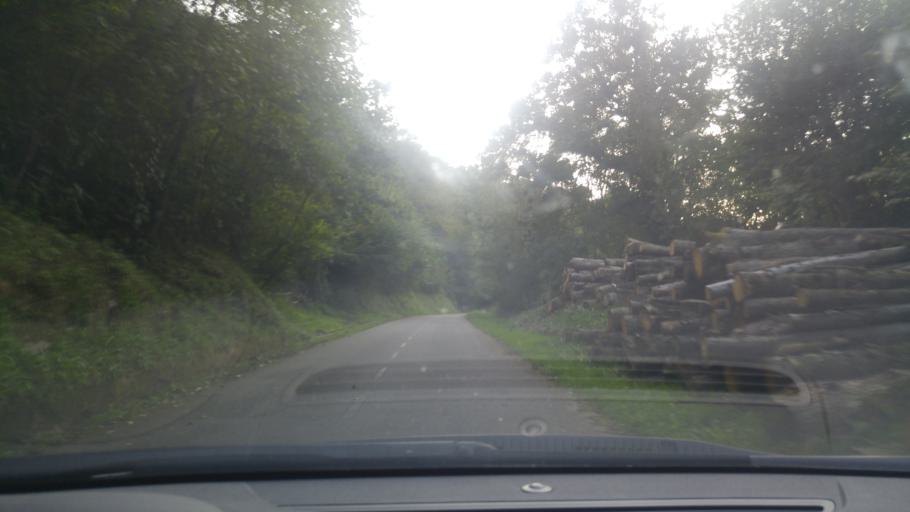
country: ES
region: Asturias
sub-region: Province of Asturias
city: Proaza
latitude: 43.2456
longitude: -6.0350
